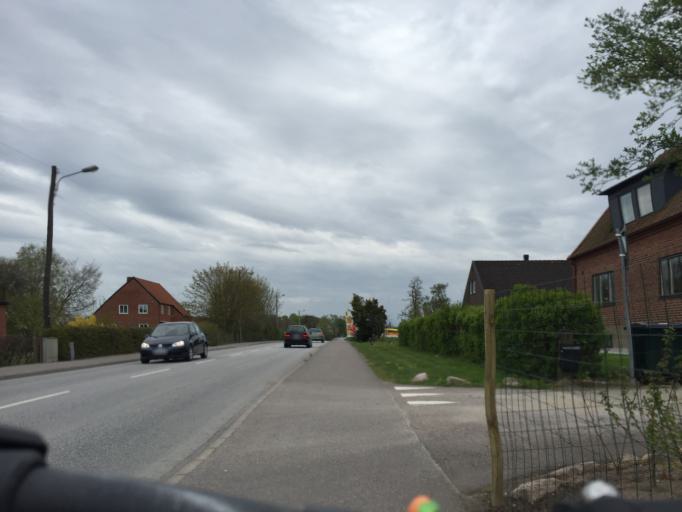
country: SE
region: Skane
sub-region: Lunds Kommun
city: Veberod
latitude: 55.6416
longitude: 13.4812
